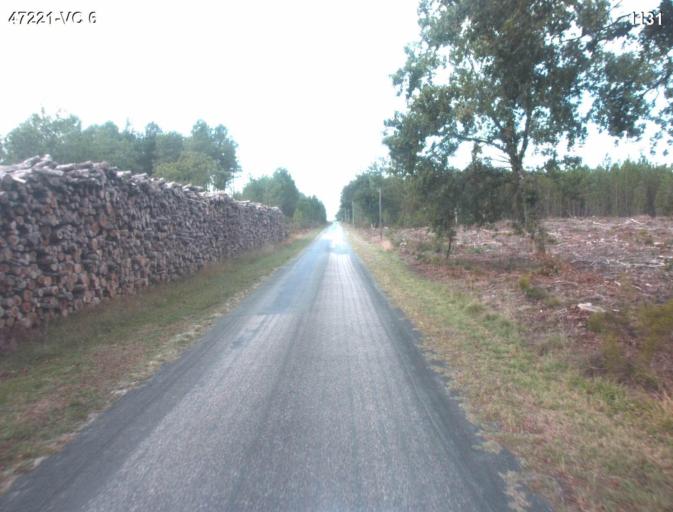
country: FR
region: Aquitaine
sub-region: Departement du Lot-et-Garonne
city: Mezin
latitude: 44.1013
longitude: 0.1673
